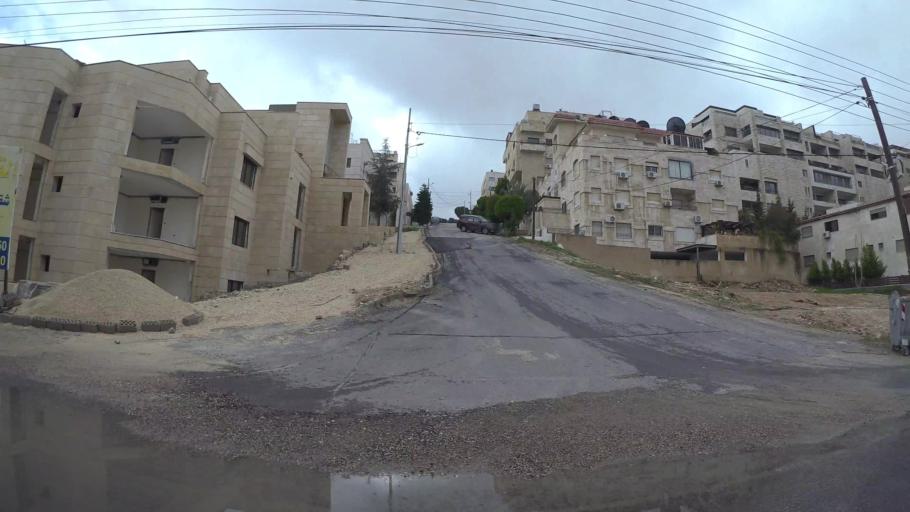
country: JO
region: Amman
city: Al Bunayyat ash Shamaliyah
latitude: 31.9420
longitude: 35.8935
